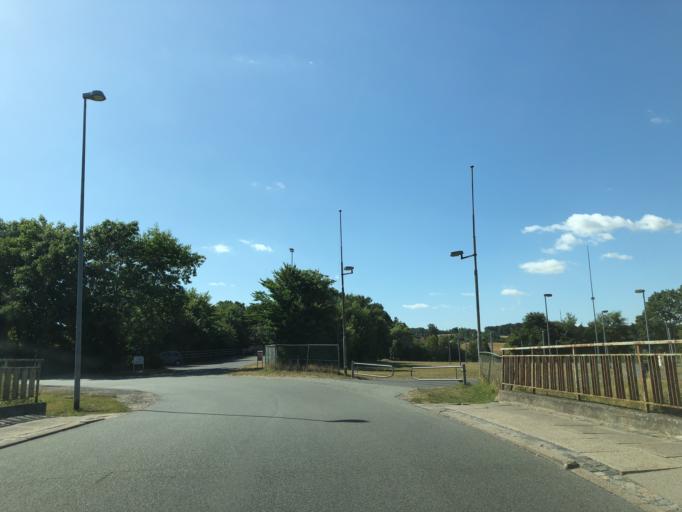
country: DK
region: North Denmark
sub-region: Mariagerfjord Kommune
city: Hobro
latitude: 56.6335
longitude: 9.7892
